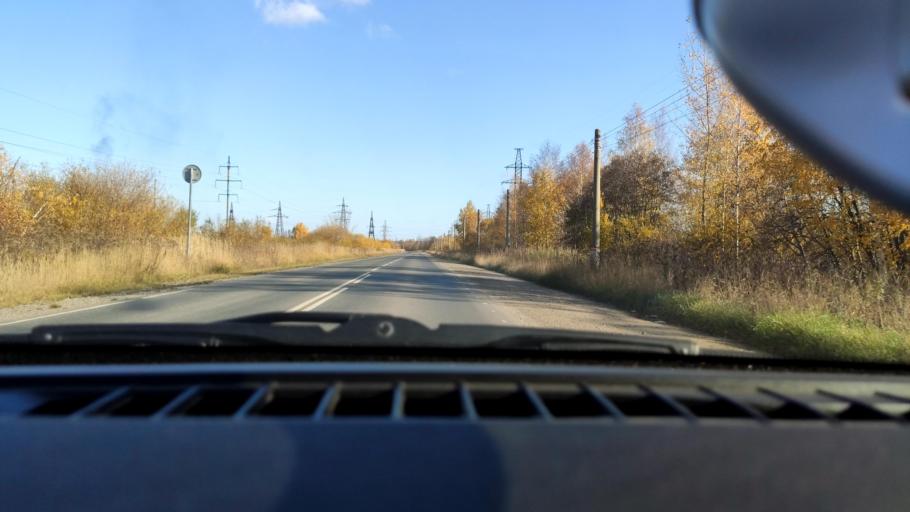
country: RU
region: Perm
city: Gamovo
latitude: 57.8917
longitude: 56.1777
